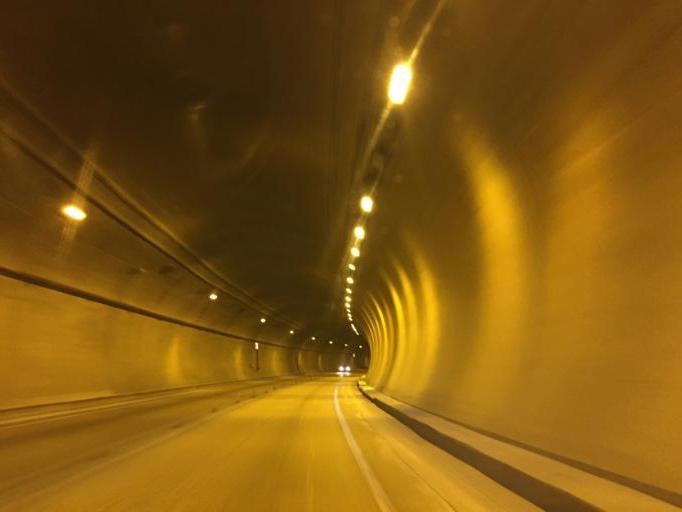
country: MX
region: Puebla
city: Xicotepec de Juarez
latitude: 20.2836
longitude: -97.9827
